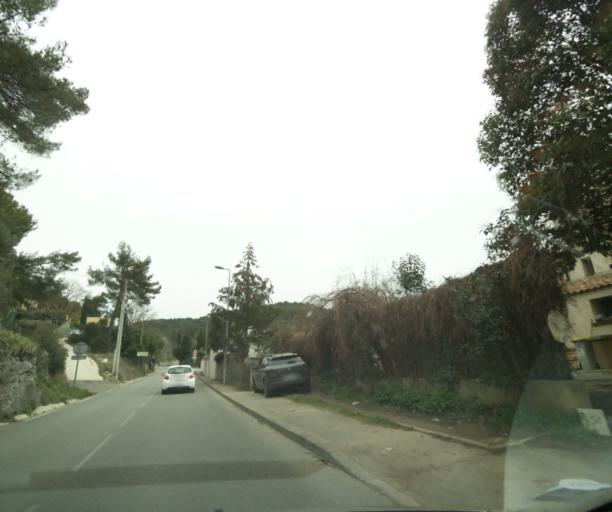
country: FR
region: Provence-Alpes-Cote d'Azur
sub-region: Departement des Bouches-du-Rhone
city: Aix-en-Provence
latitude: 43.5352
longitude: 5.4783
